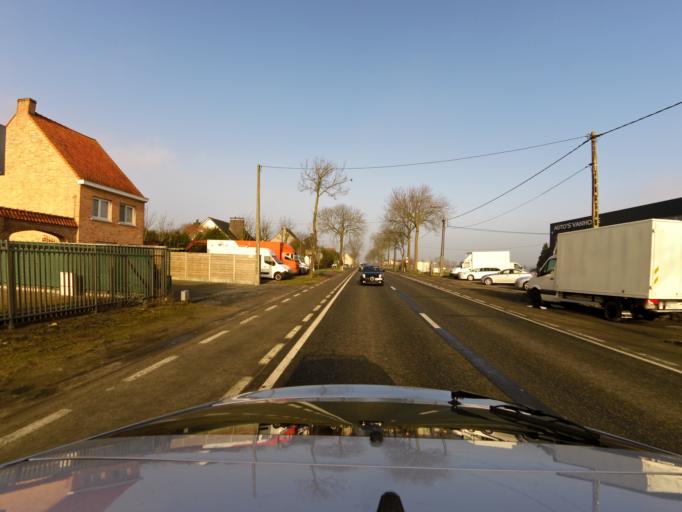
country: BE
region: Flanders
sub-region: Provincie West-Vlaanderen
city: Ichtegem
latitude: 51.0916
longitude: 3.0479
